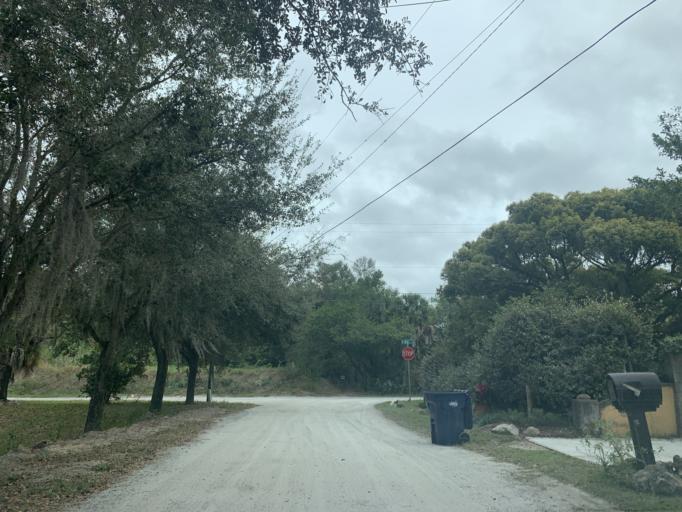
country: US
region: Florida
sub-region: Hillsborough County
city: East Lake-Orient Park
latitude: 27.9760
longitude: -82.4063
